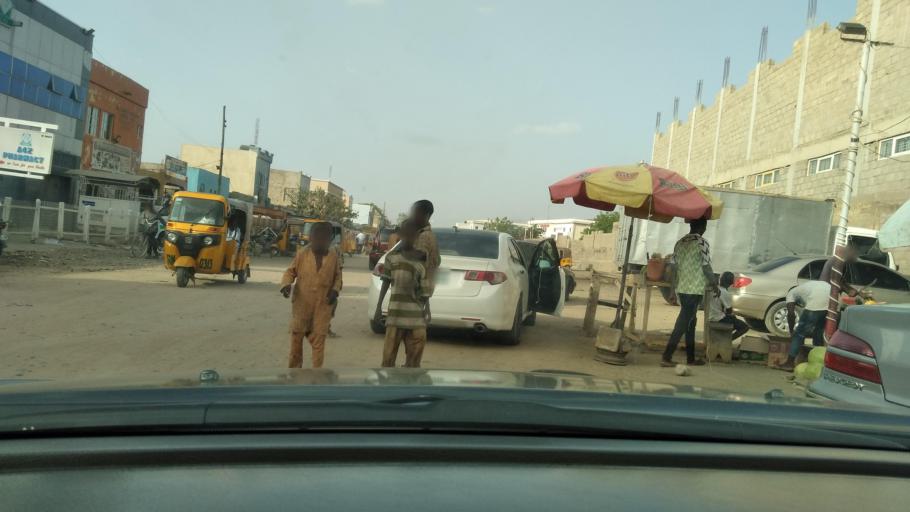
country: NG
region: Kano
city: Kano
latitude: 11.9784
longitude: 8.5640
